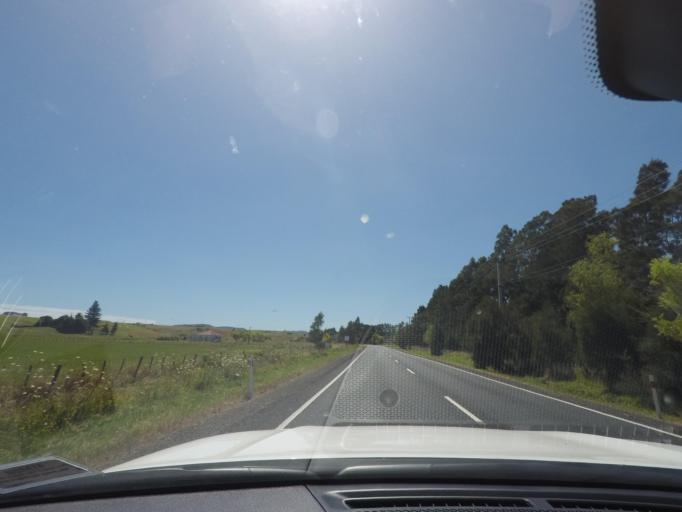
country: NZ
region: Auckland
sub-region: Auckland
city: Parakai
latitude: -36.6370
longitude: 174.3847
